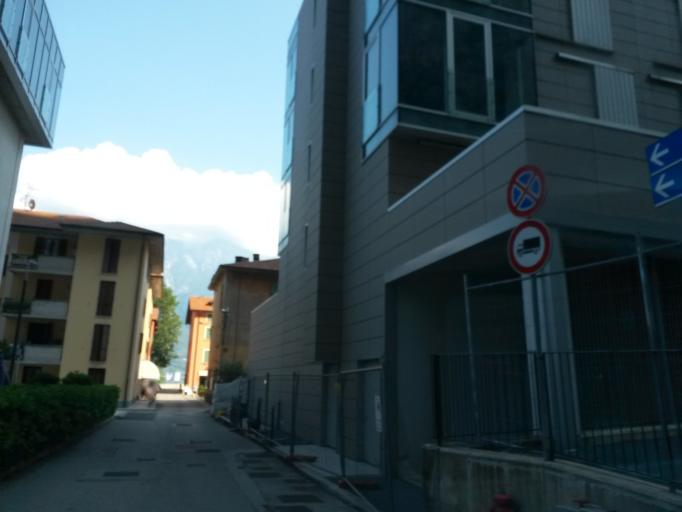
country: IT
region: Lombardy
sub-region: Provincia di Brescia
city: Pieve
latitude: 45.7553
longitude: 10.7495
